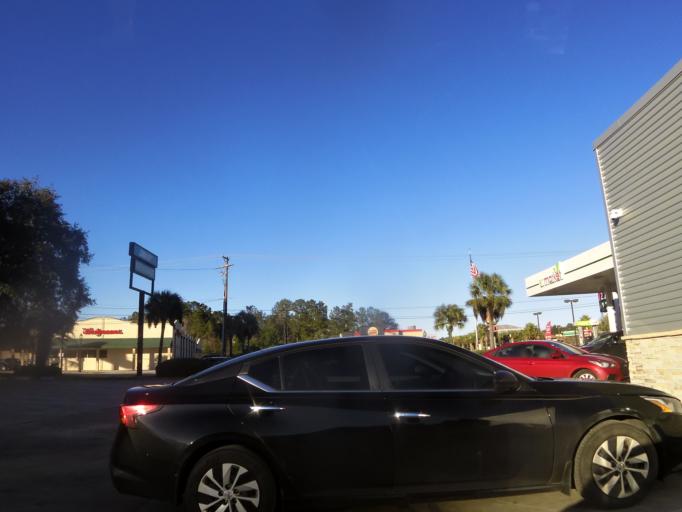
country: US
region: South Carolina
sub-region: Jasper County
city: Ridgeland
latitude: 32.4779
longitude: -80.9737
